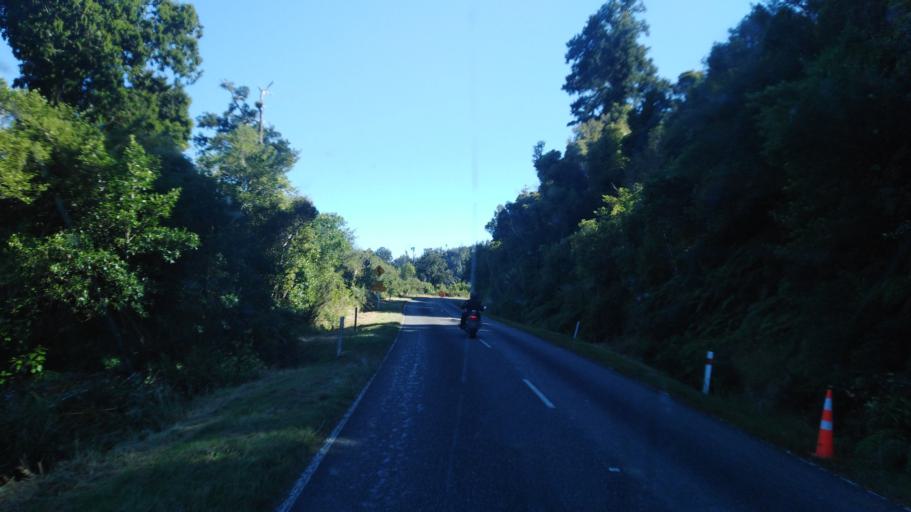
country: NZ
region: West Coast
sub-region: Buller District
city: Westport
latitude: -41.5336
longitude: 171.9927
